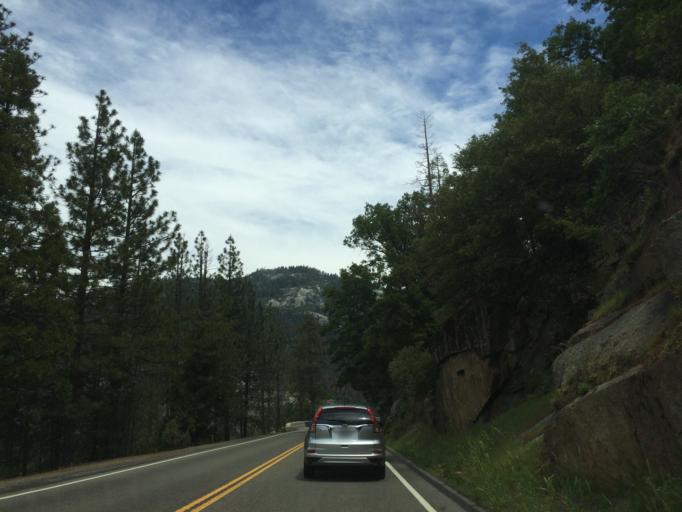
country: US
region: California
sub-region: Mariposa County
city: Yosemite Valley
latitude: 37.7156
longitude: -119.7076
